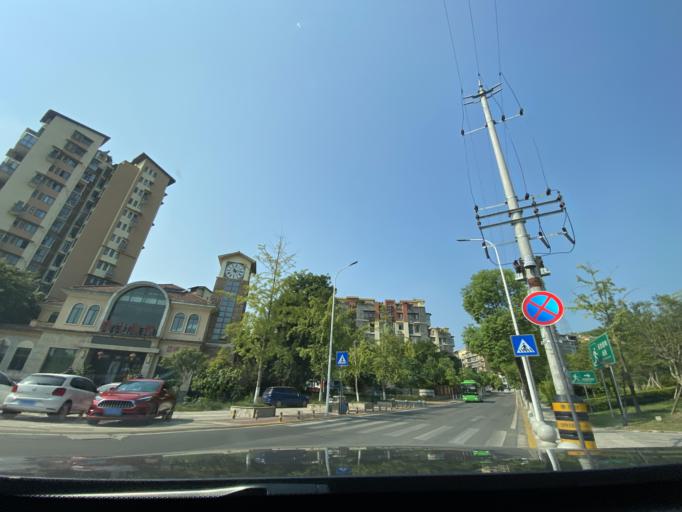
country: CN
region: Sichuan
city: Jiancheng
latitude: 30.4163
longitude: 104.5431
